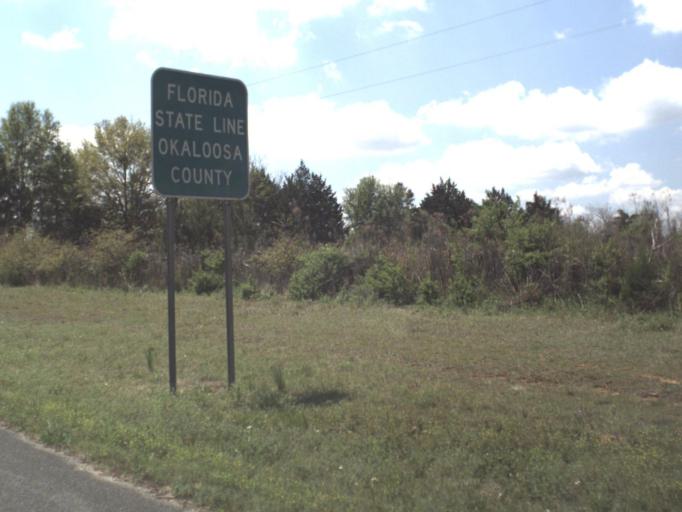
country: US
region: Florida
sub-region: Okaloosa County
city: Crestview
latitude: 30.9946
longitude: -86.6279
